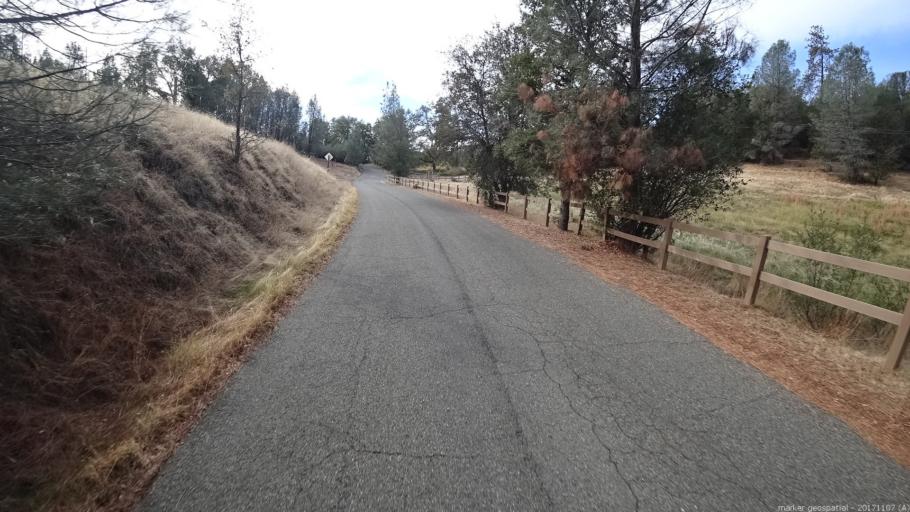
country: US
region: California
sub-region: Shasta County
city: Shasta
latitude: 40.5129
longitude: -122.5487
